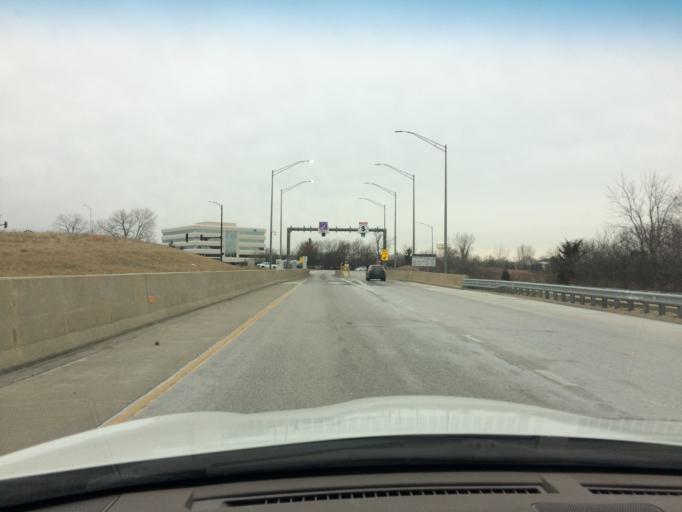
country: US
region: Illinois
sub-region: Kane County
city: North Aurora
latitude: 41.7997
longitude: -88.2806
